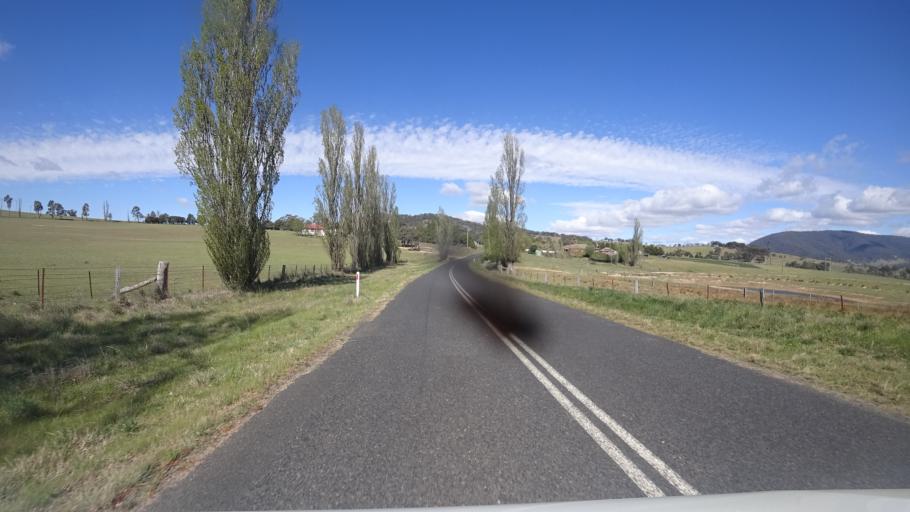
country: AU
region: New South Wales
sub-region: Lithgow
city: Portland
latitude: -33.5223
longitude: 149.9446
